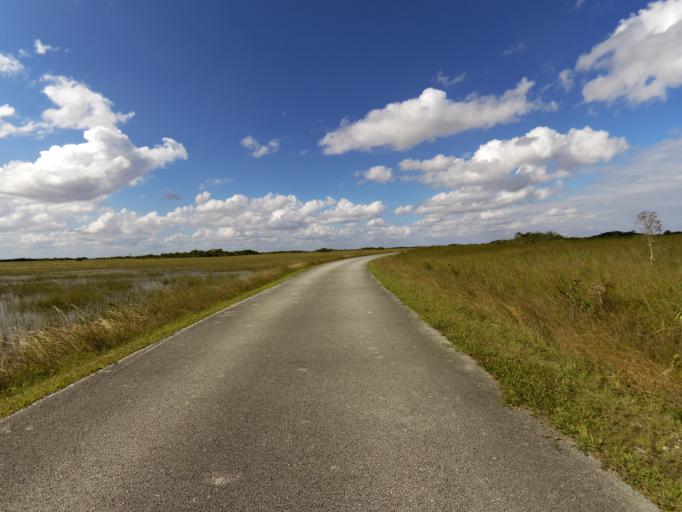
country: US
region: Florida
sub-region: Miami-Dade County
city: The Hammocks
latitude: 25.7282
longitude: -80.7593
